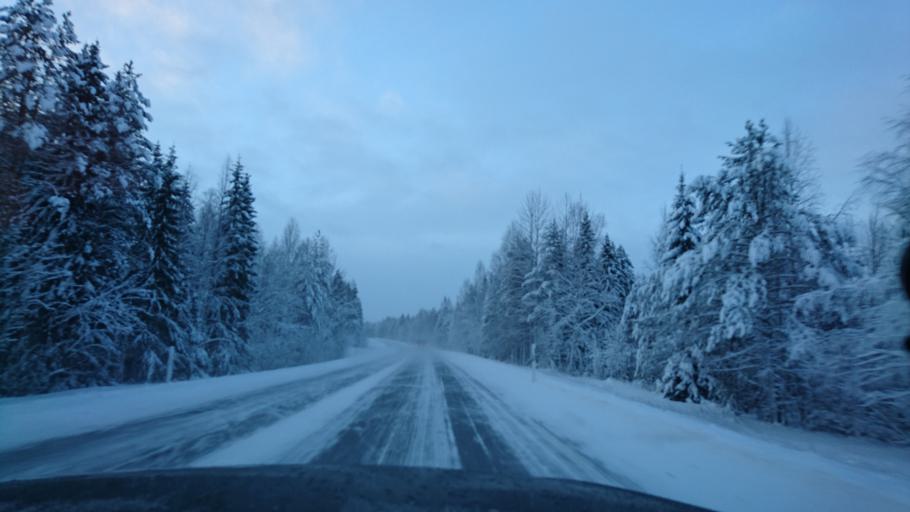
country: FI
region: Kainuu
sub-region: Kehys-Kainuu
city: Puolanka
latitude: 65.4661
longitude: 27.6568
